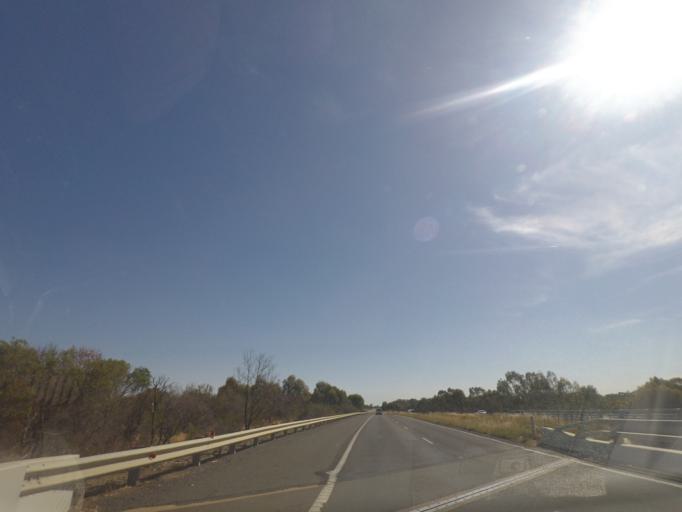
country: AU
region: Victoria
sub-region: Greater Shepparton
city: Shepparton
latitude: -36.6125
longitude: 145.3164
